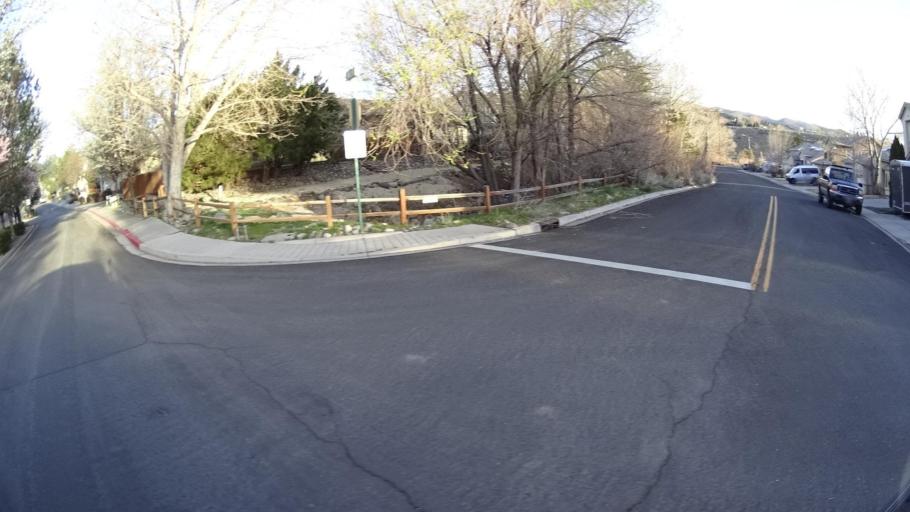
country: US
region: Nevada
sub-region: Washoe County
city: Mogul
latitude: 39.5056
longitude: -119.9038
